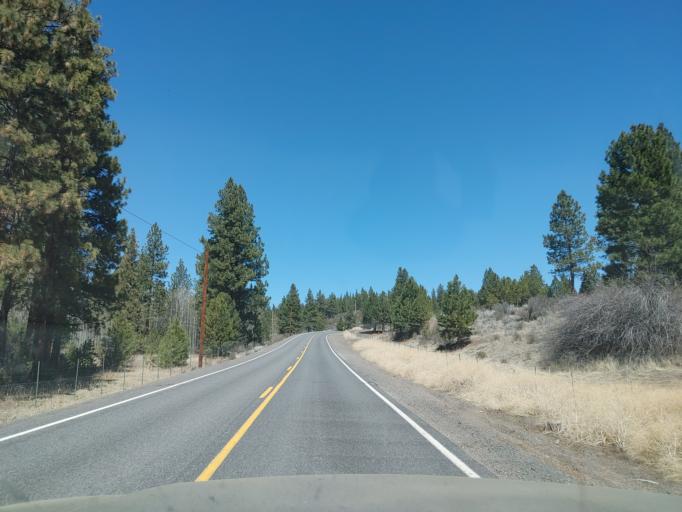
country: US
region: Oregon
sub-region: Klamath County
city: Klamath Falls
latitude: 42.5563
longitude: -121.8943
